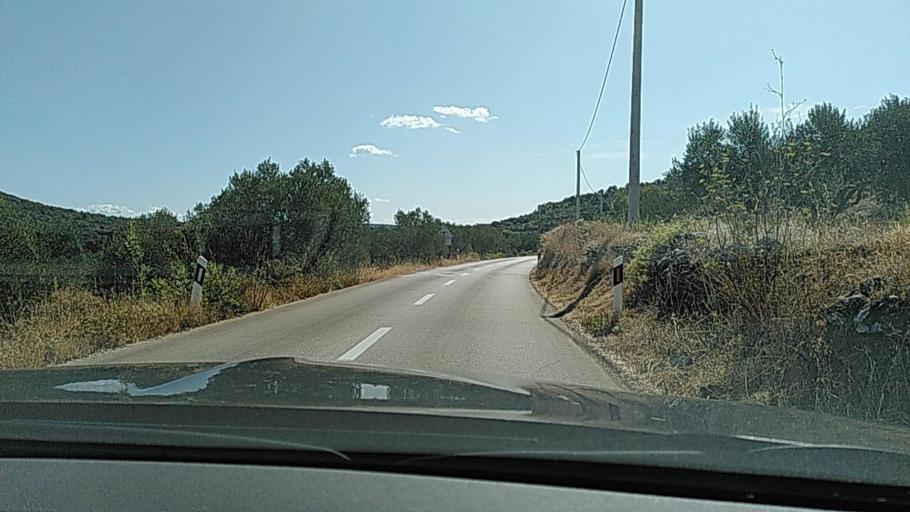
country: HR
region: Splitsko-Dalmatinska
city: Jelsa
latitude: 43.1441
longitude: 16.8420
